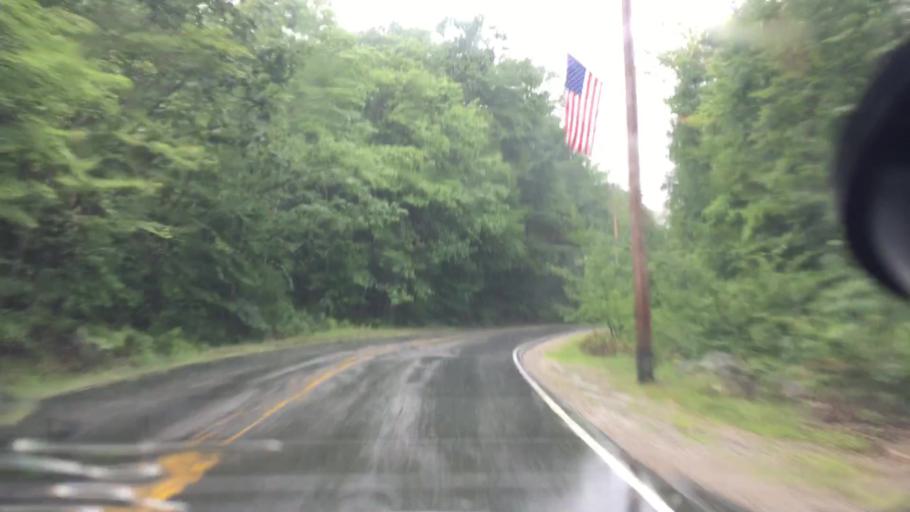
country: US
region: Maine
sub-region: Oxford County
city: Lovell
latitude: 44.2567
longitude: -70.8317
